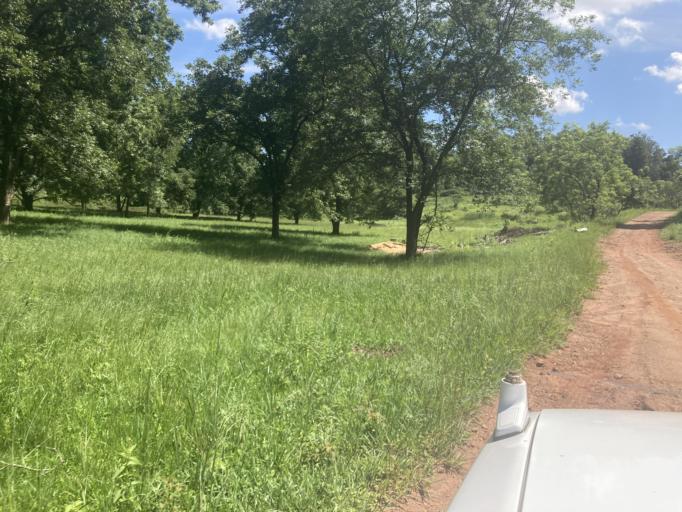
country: SZ
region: Hhohho
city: Lobamba
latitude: -26.4895
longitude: 31.1898
